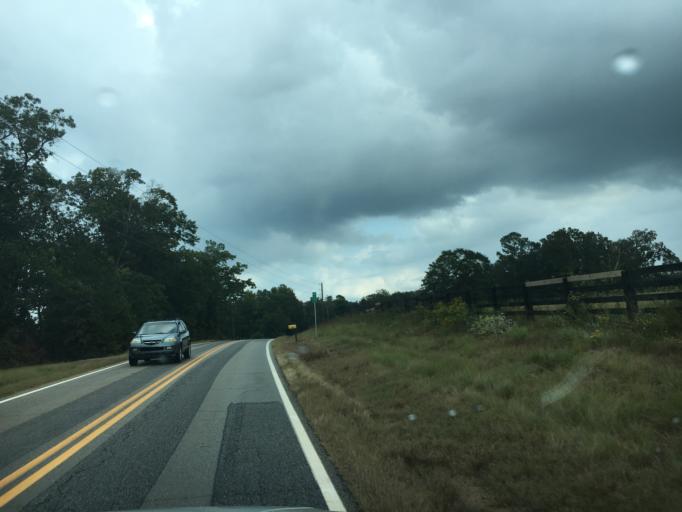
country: US
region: Georgia
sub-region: Hart County
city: Reed Creek
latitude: 34.4382
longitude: -82.9314
